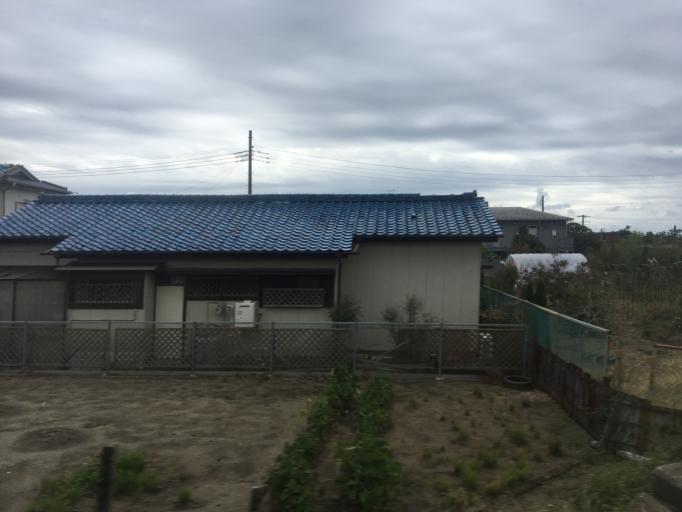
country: JP
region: Chiba
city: Kawaguchi
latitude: 35.1186
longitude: 140.1151
